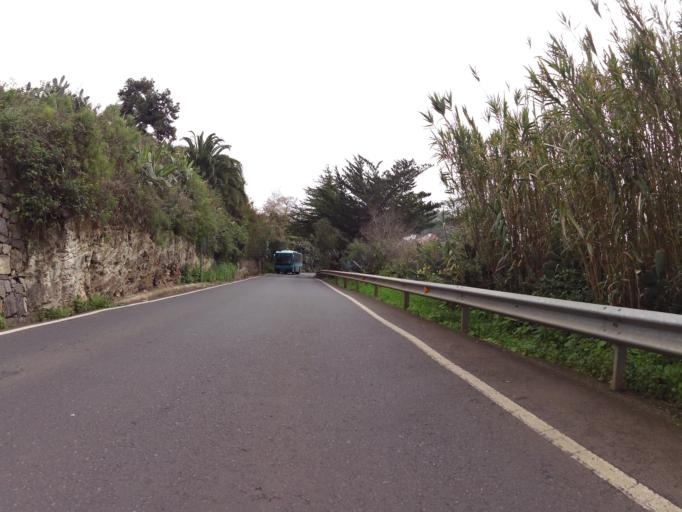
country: ES
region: Canary Islands
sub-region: Provincia de Las Palmas
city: Teror
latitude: 28.0867
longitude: -15.5415
